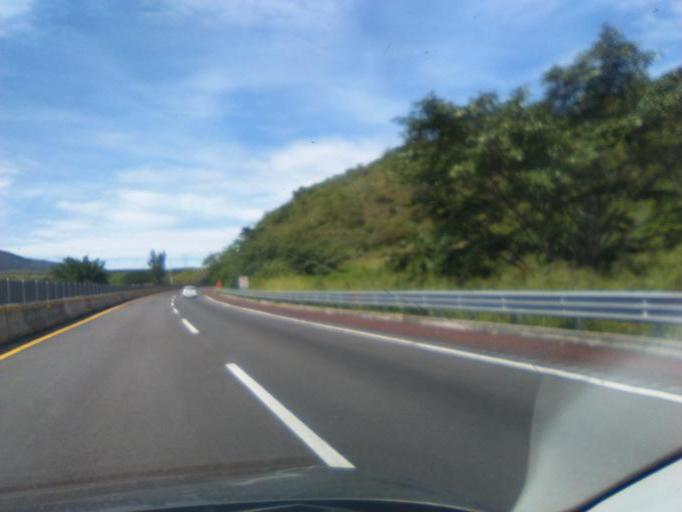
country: MX
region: Guerrero
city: Mazatlan
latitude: 17.4095
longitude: -99.4637
